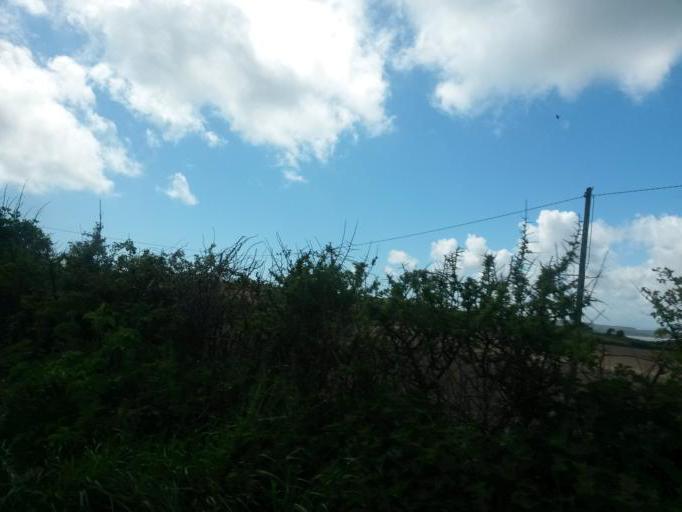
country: IE
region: Munster
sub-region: Waterford
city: Dunmore East
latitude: 52.1938
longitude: -6.8994
